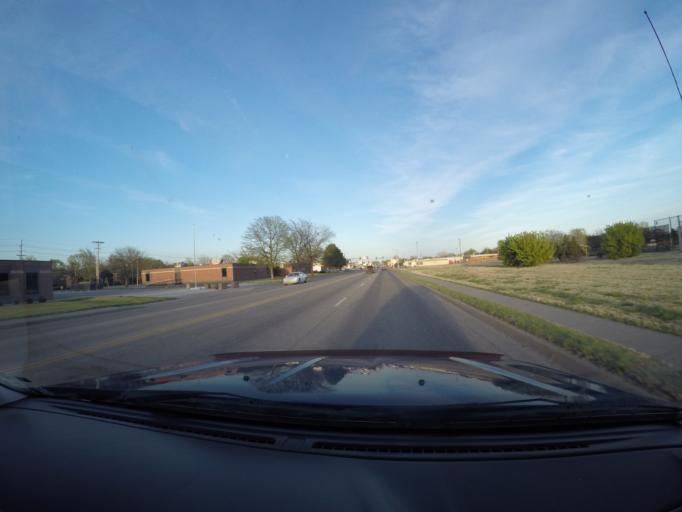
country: US
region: Kansas
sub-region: Saline County
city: Salina
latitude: 38.8271
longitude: -97.6004
